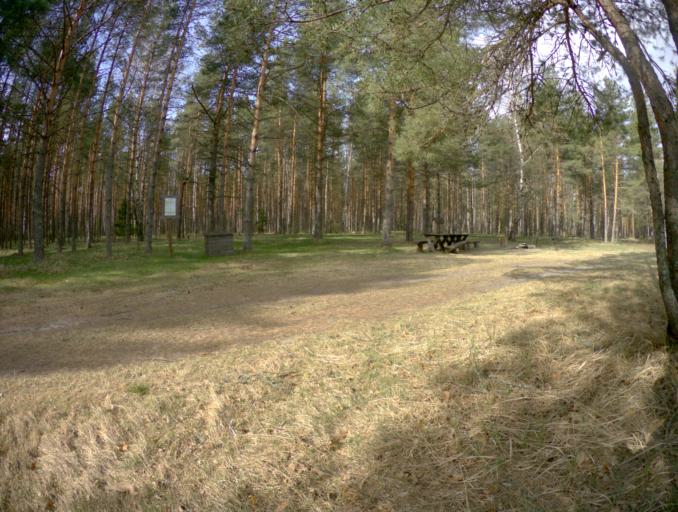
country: RU
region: Vladimir
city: Mezinovskiy
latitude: 55.6074
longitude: 40.3981
